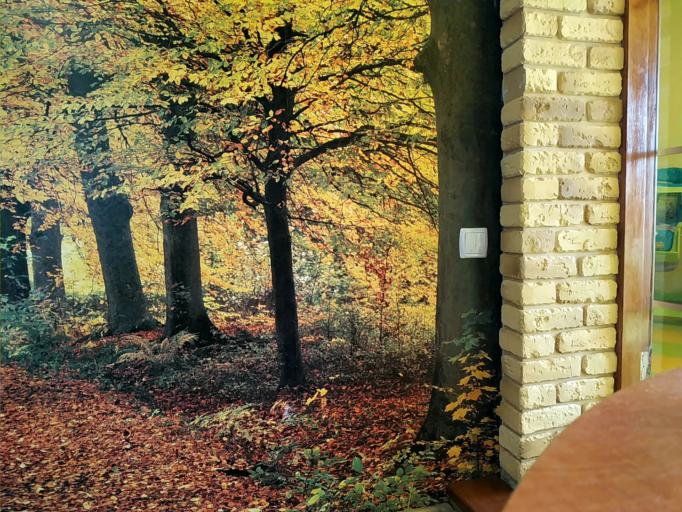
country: RU
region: Novgorod
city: Staraya Russa
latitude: 57.8325
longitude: 31.4850
